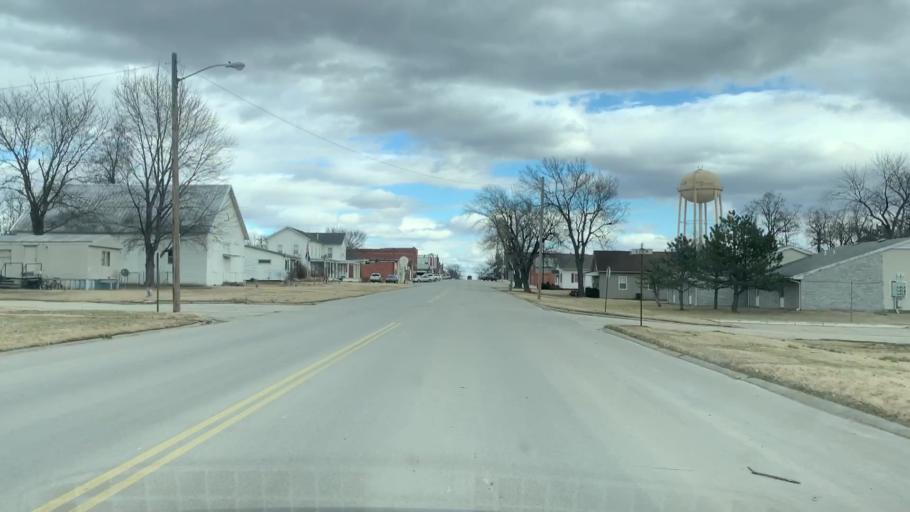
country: US
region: Kansas
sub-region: Allen County
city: Humboldt
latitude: 37.8112
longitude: -95.4411
